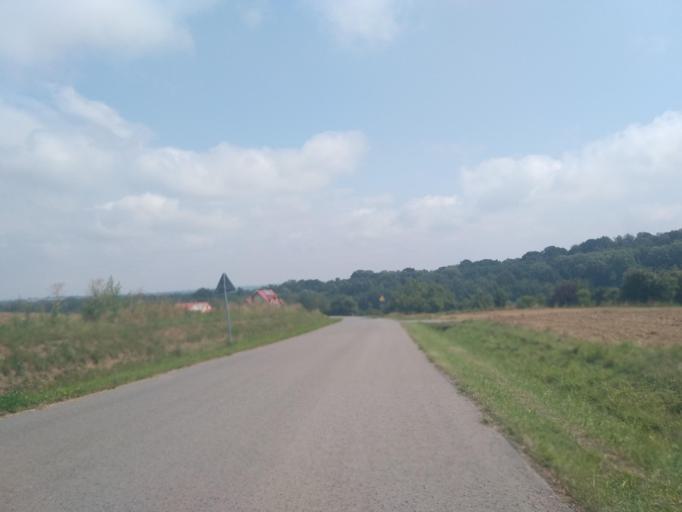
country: PL
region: Subcarpathian Voivodeship
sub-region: Powiat lancucki
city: Kraczkowa
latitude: 50.0270
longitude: 22.1616
